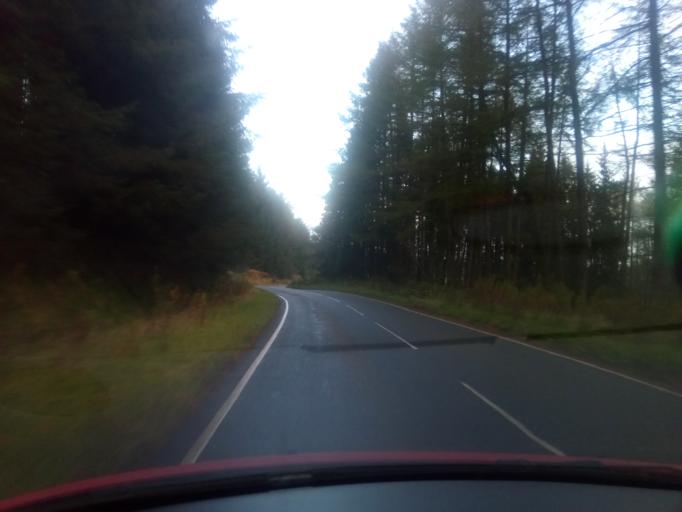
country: GB
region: Scotland
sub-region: The Scottish Borders
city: Hawick
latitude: 55.3351
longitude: -2.6486
